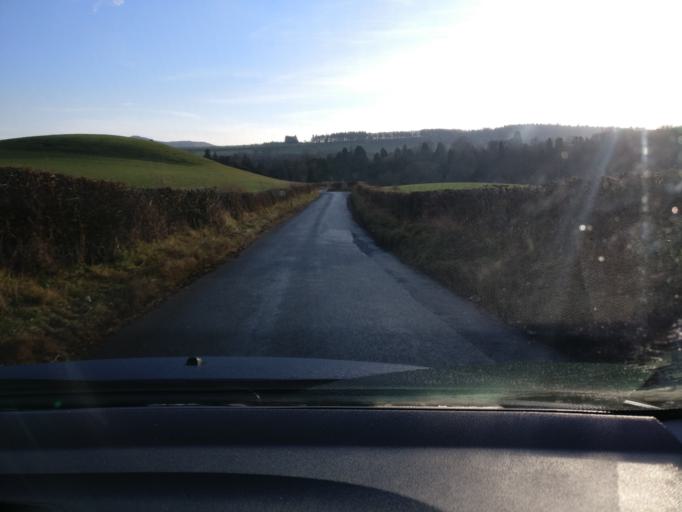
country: GB
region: Scotland
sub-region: The Scottish Borders
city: Hawick
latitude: 55.4446
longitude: -2.7456
